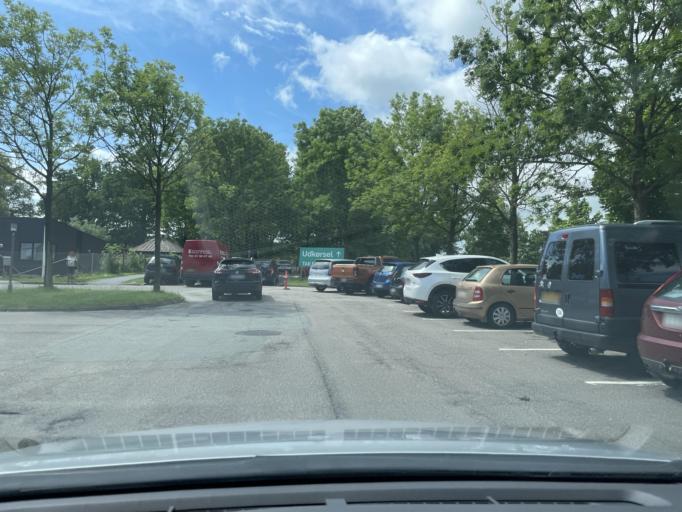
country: DK
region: South Denmark
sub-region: Odense Kommune
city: Odense
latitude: 55.3619
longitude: 10.3580
